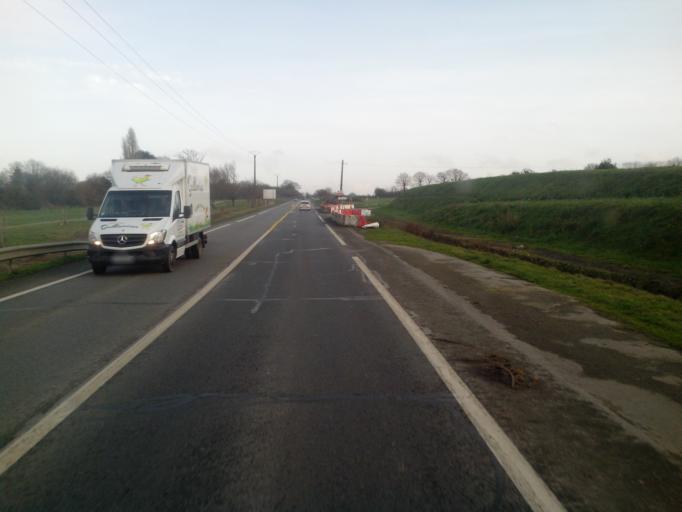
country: FR
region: Brittany
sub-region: Departement du Morbihan
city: Ploermel
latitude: 47.9424
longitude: -2.3956
